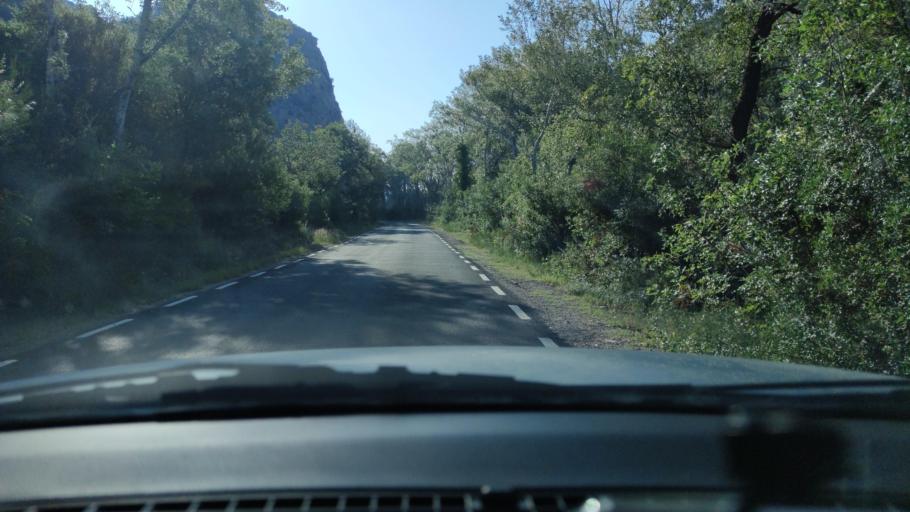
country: ES
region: Catalonia
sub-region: Provincia de Lleida
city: Camarasa
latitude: 41.8727
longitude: 0.8539
